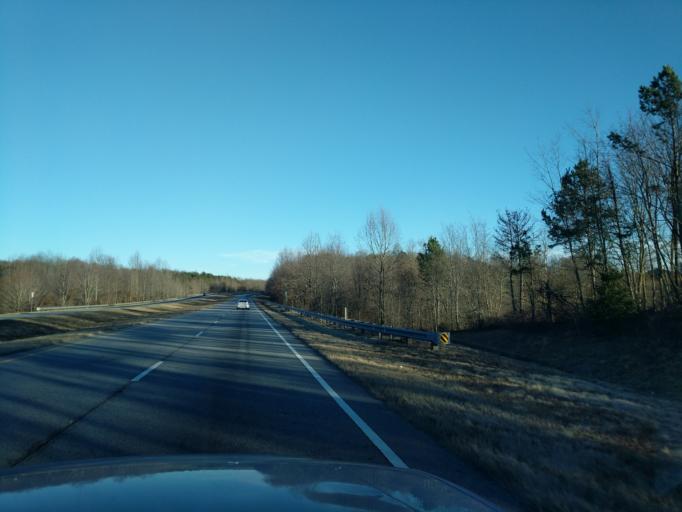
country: US
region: Georgia
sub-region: Stephens County
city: Toccoa
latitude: 34.5936
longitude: -83.4243
